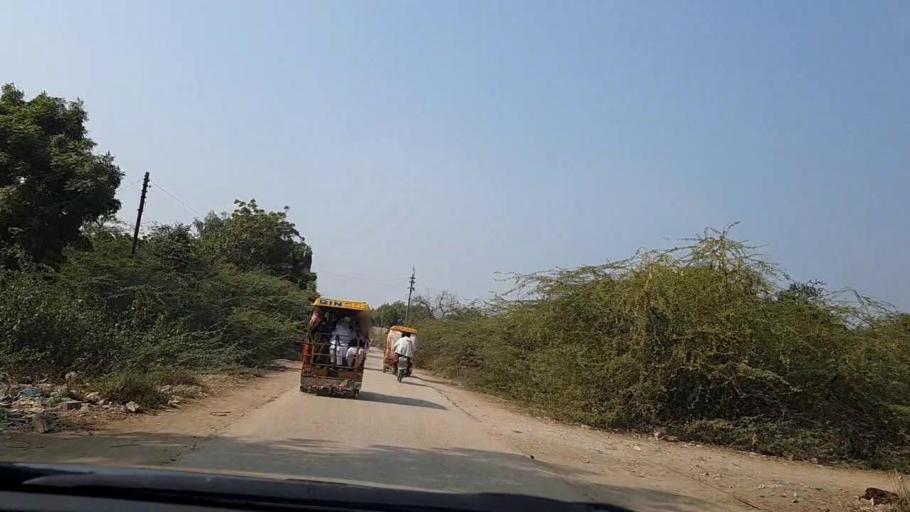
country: PK
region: Sindh
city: Sakrand
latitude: 26.1413
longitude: 68.2755
